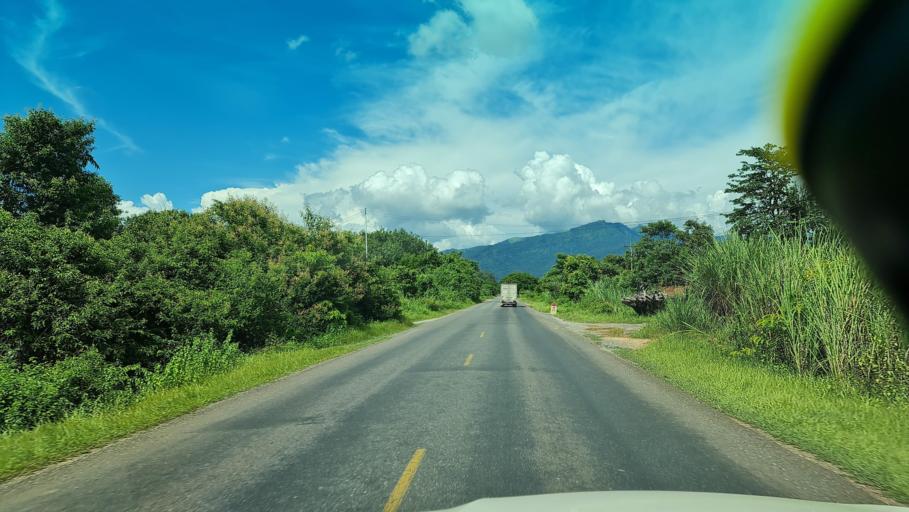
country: LA
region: Bolikhamxai
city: Pakkading
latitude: 18.2953
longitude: 104.0877
